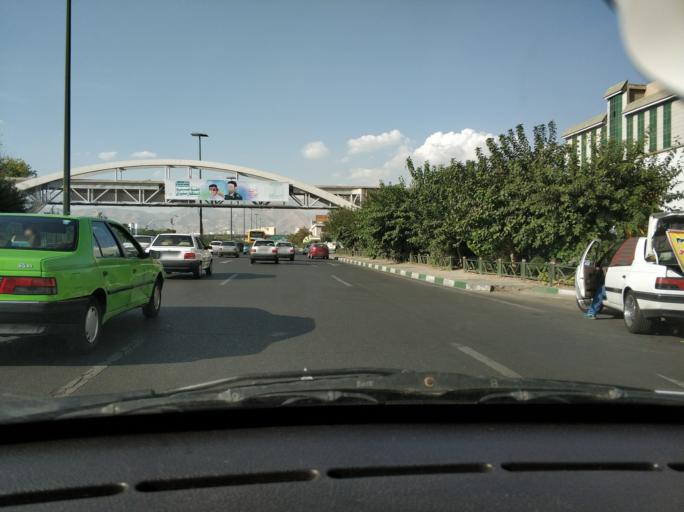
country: IR
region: Tehran
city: Tehran
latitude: 35.7052
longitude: 51.3375
